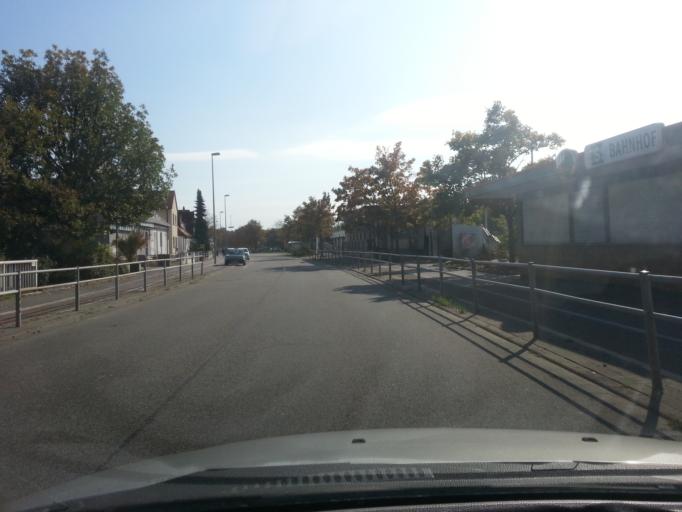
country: DE
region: Rheinland-Pfalz
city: Schifferstadt
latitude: 49.3748
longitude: 8.3770
